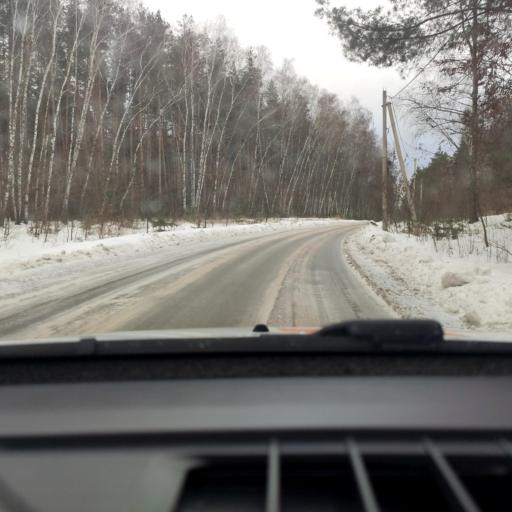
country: RU
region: Voronezj
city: Podgornoye
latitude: 51.7513
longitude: 39.1566
